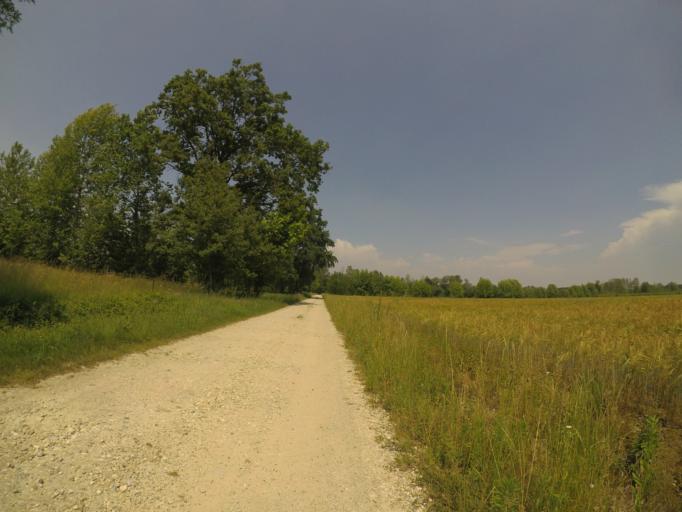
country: IT
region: Friuli Venezia Giulia
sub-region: Provincia di Udine
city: Bertiolo
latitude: 45.9196
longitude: 13.0384
